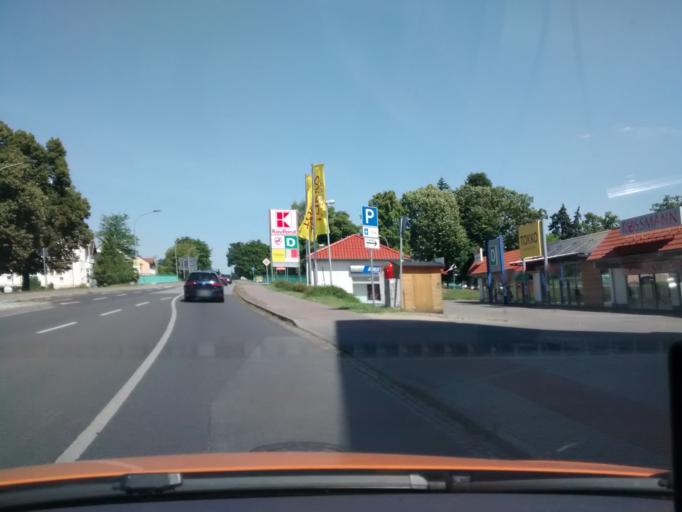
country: DE
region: Brandenburg
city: Hohen Neuendorf
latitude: 52.6716
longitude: 13.2800
